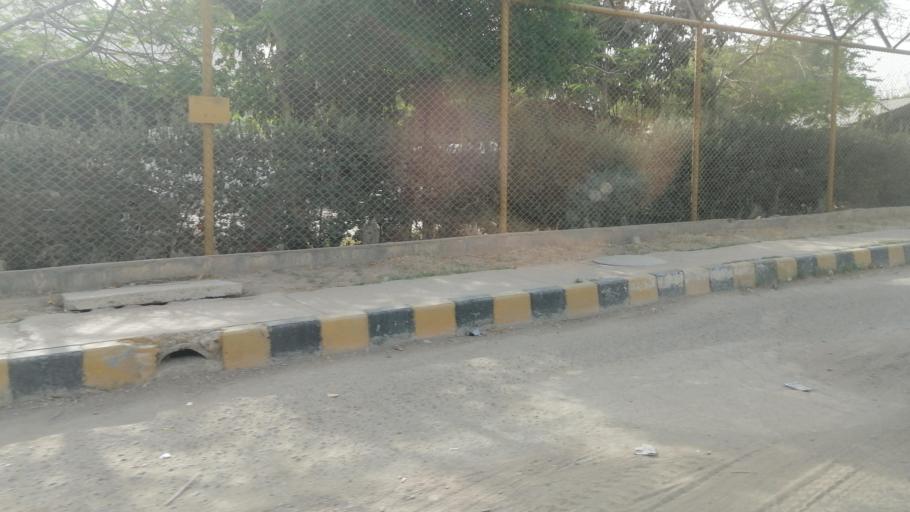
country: PK
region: Sindh
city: Malir Cantonment
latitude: 24.8925
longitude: 67.1781
